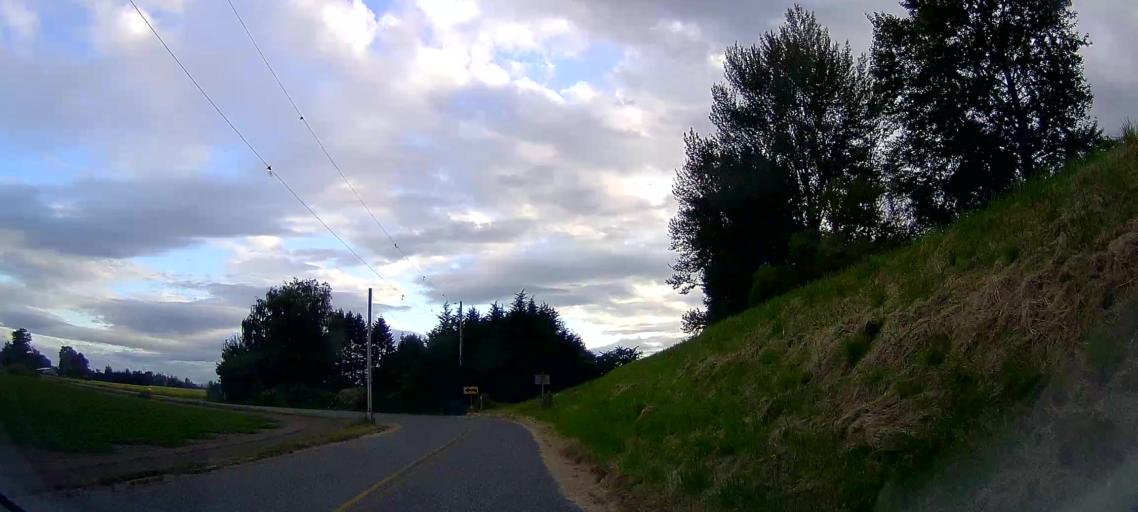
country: US
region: Washington
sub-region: Skagit County
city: Mount Vernon
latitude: 48.3799
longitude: -122.3784
